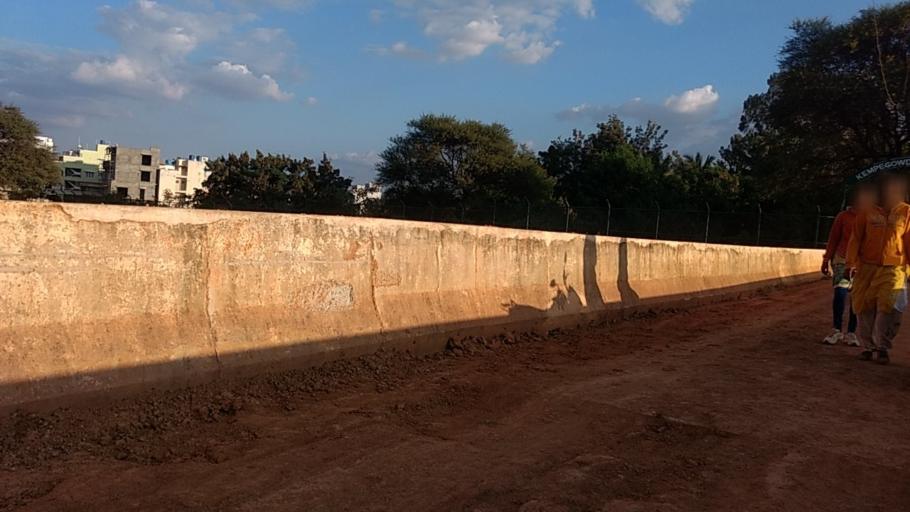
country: IN
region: Karnataka
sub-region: Bangalore Urban
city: Yelahanka
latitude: 13.0633
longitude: 77.5677
